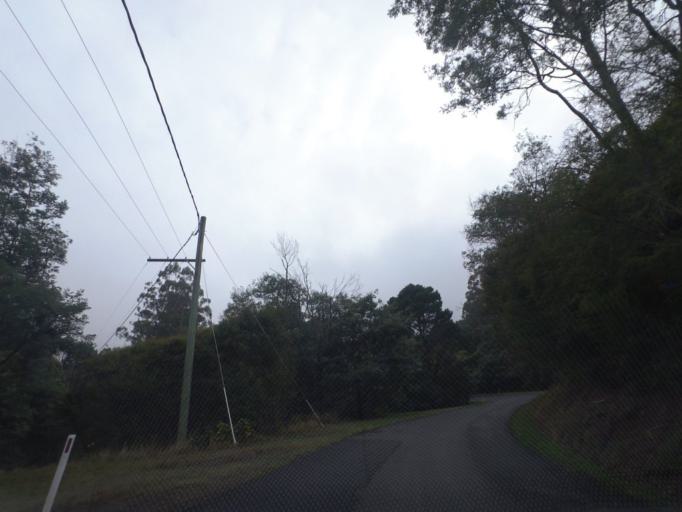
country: AU
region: Victoria
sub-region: Yarra Ranges
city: Launching Place
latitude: -37.7307
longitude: 145.5927
